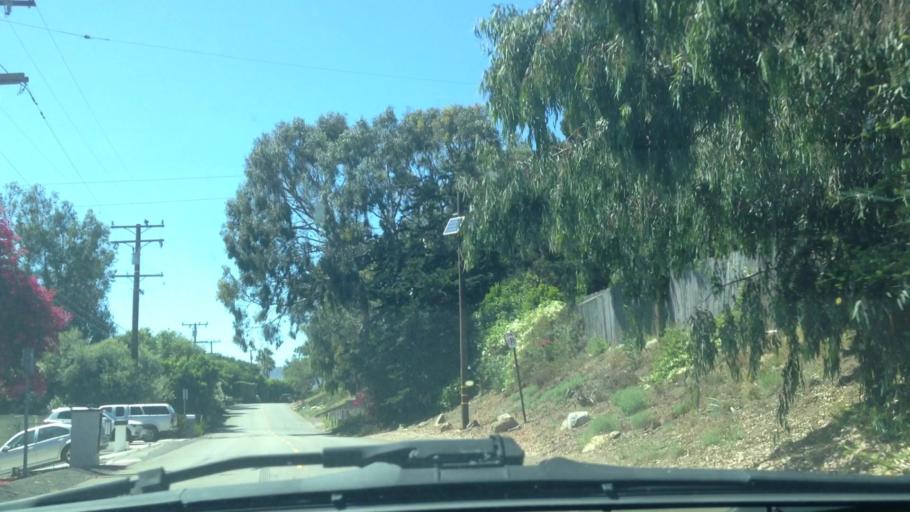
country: US
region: California
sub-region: Los Angeles County
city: Malibu
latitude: 34.0079
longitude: -118.8114
